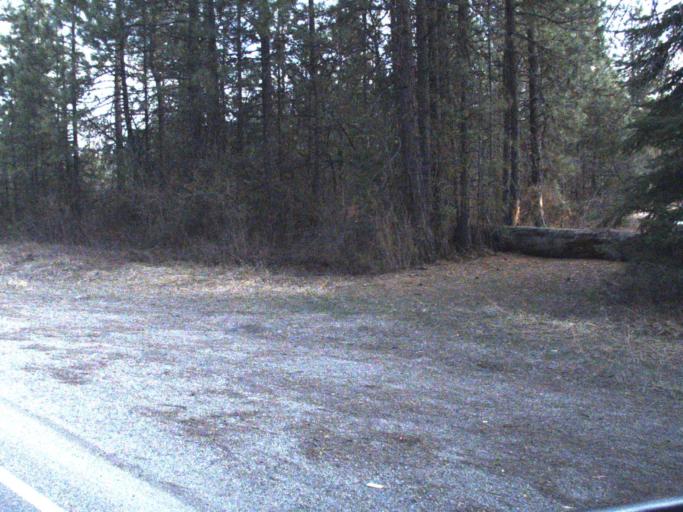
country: US
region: Washington
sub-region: Pend Oreille County
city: Newport
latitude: 48.3144
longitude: -117.2900
